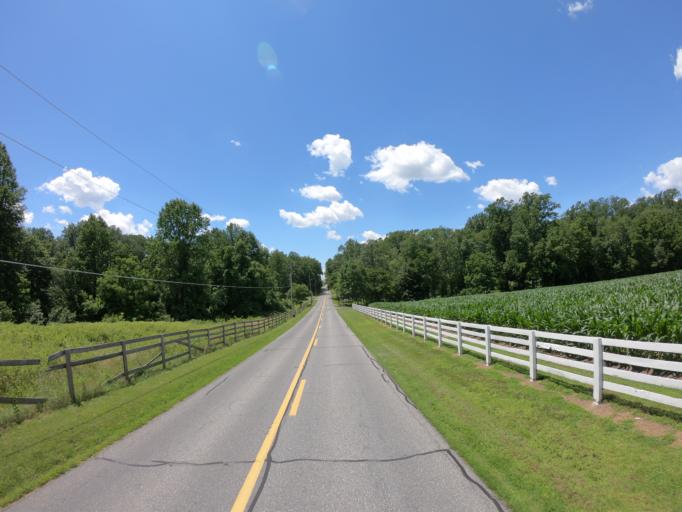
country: US
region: Delaware
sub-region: New Castle County
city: Middletown
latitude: 39.4812
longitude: -75.7622
